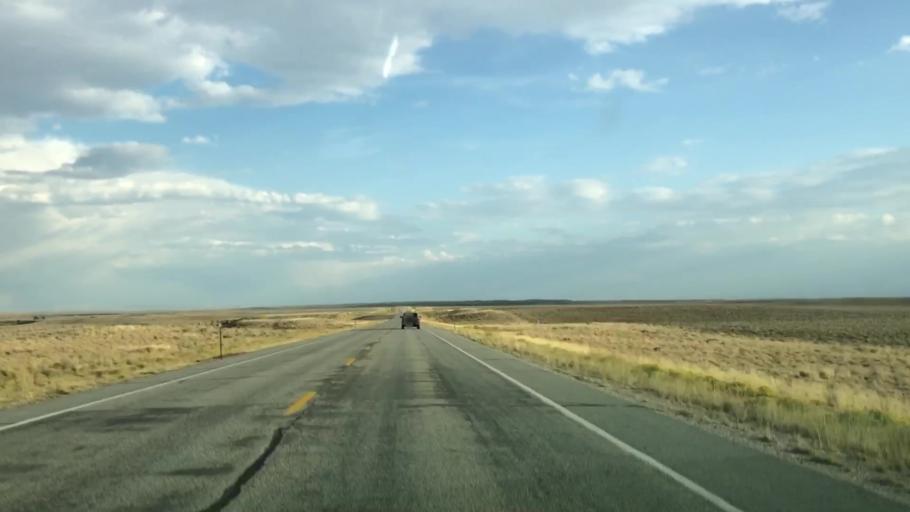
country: US
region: Wyoming
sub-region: Sublette County
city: Marbleton
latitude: 42.3313
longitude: -109.5163
